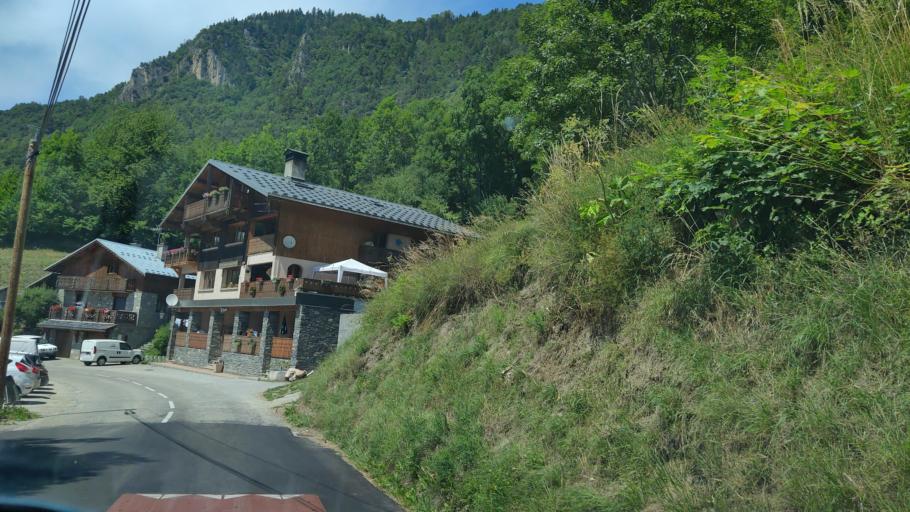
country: FR
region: Rhone-Alpes
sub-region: Departement de la Savoie
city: Les Allues
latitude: 45.4542
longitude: 6.5953
